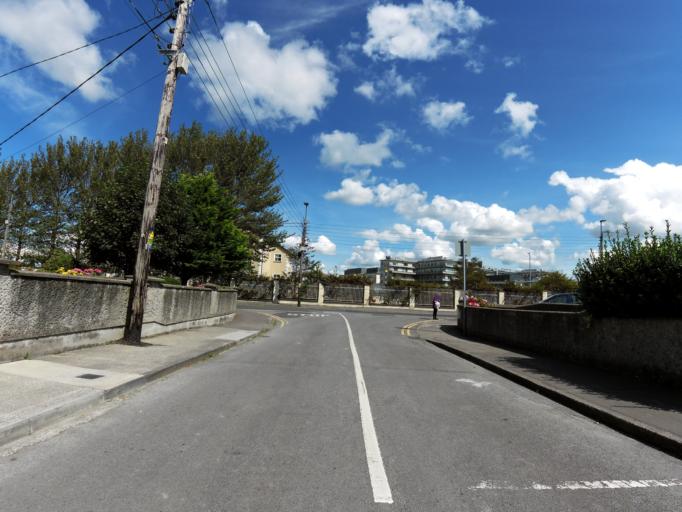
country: IE
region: Connaught
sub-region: County Galway
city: Gaillimh
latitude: 53.2750
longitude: -9.0685
